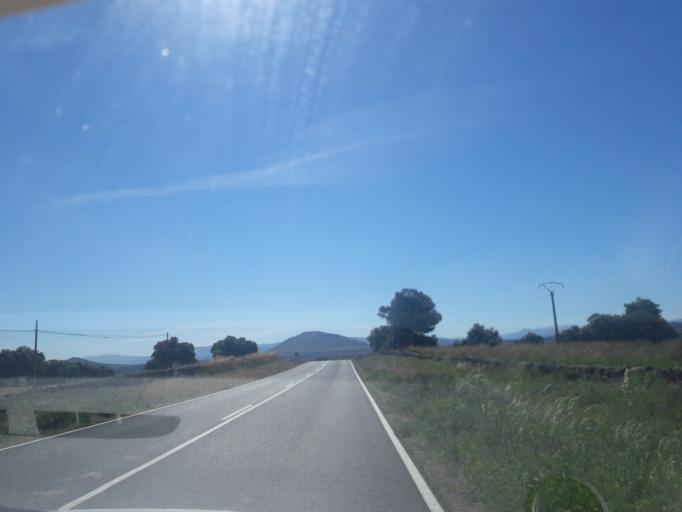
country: ES
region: Castille and Leon
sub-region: Provincia de Salamanca
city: Santibanez de Bejar
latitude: 40.4816
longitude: -5.6432
